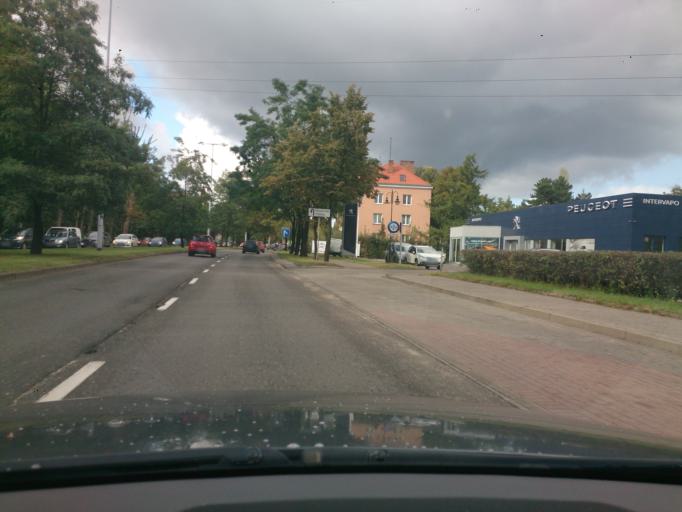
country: PL
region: Pomeranian Voivodeship
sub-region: Sopot
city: Sopot
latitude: 54.4248
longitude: 18.5636
